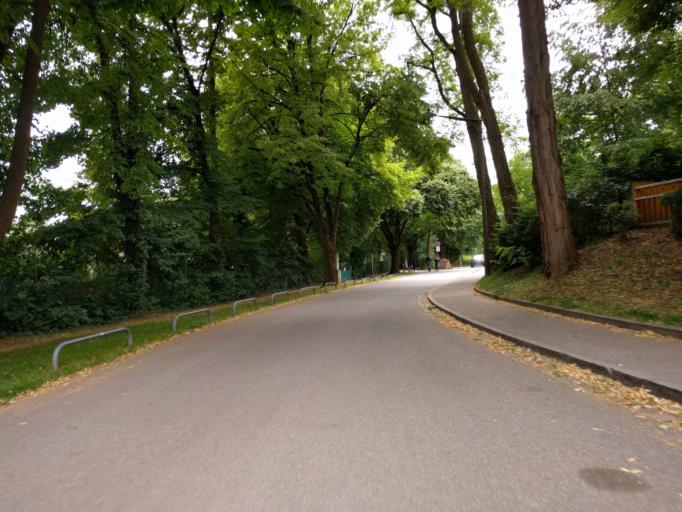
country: DE
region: Bavaria
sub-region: Upper Palatinate
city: Lappersdorf
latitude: 49.0236
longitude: 12.0875
